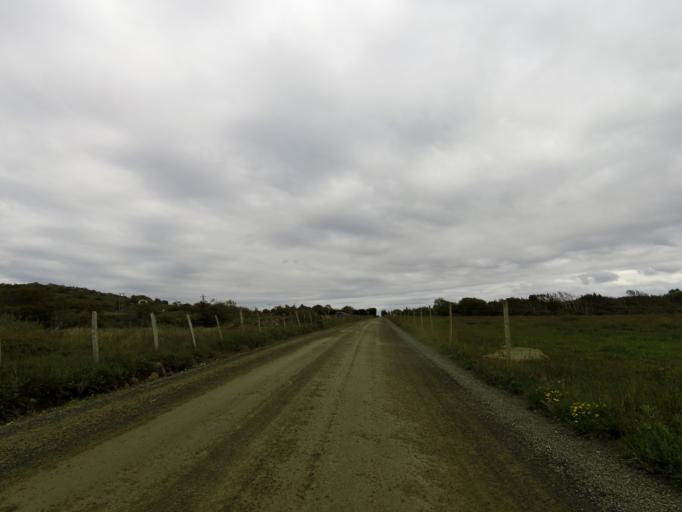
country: NO
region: Vest-Agder
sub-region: Farsund
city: Vestbygd
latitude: 58.1320
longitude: 6.6097
